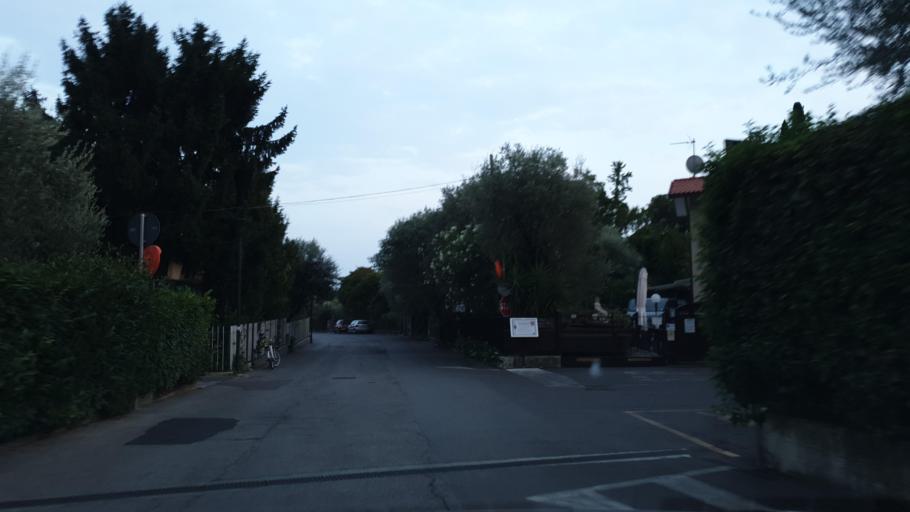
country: IT
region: Lombardy
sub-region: Provincia di Brescia
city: Toscolano Maderno
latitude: 45.6407
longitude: 10.6126
